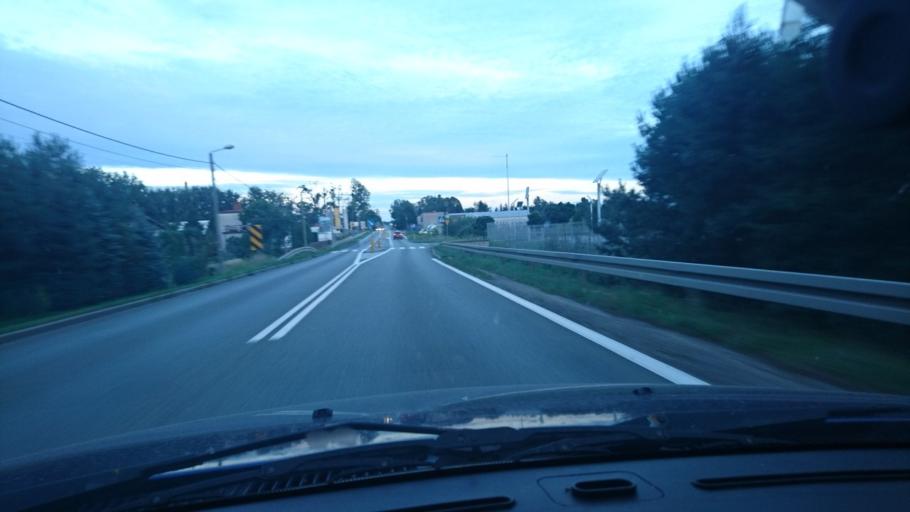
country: PL
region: Silesian Voivodeship
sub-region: Powiat tarnogorski
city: Tarnowskie Gory
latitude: 50.4685
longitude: 18.8101
